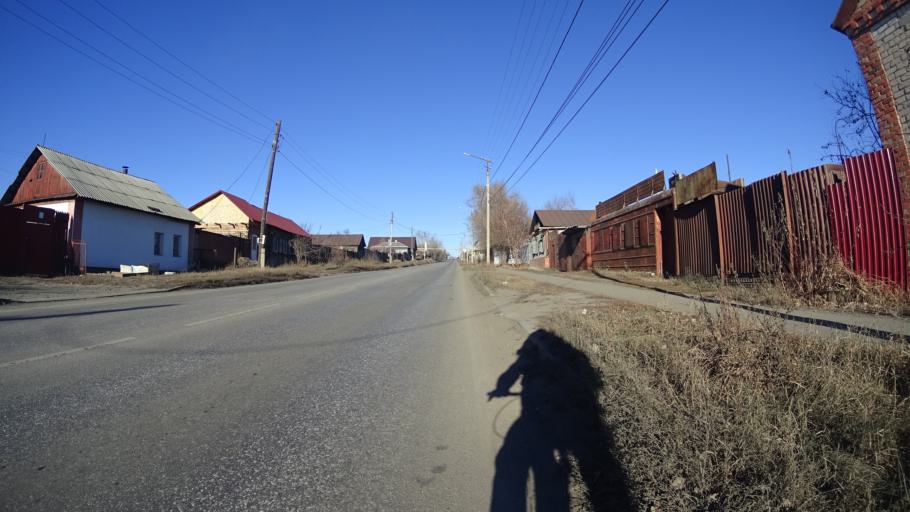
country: RU
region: Chelyabinsk
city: Troitsk
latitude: 54.0987
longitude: 61.5628
